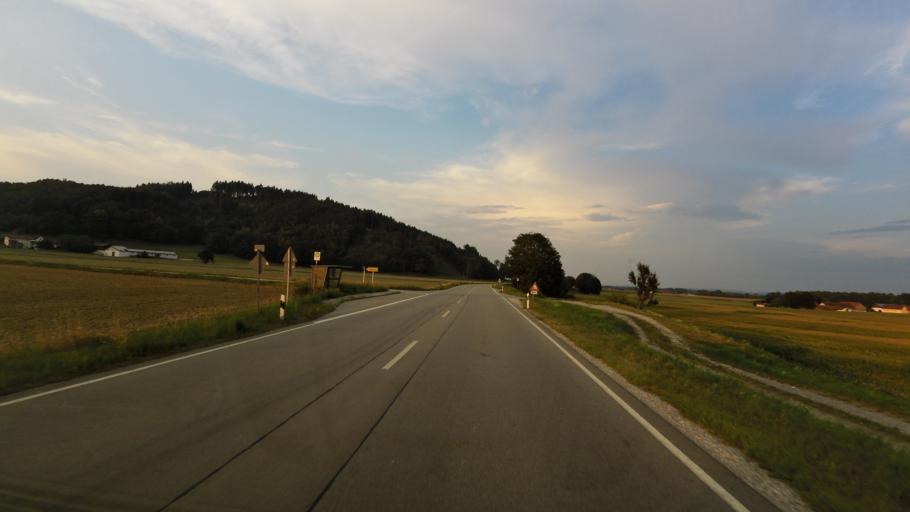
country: DE
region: Bavaria
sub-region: Lower Bavaria
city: Stubenberg
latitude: 48.2925
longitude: 13.1038
